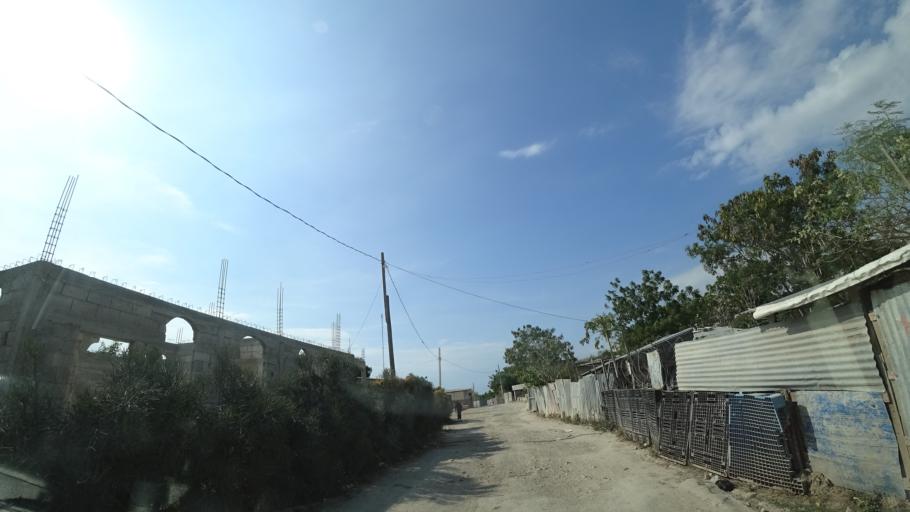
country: HT
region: Ouest
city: Croix des Bouquets
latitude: 18.6570
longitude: -72.2841
